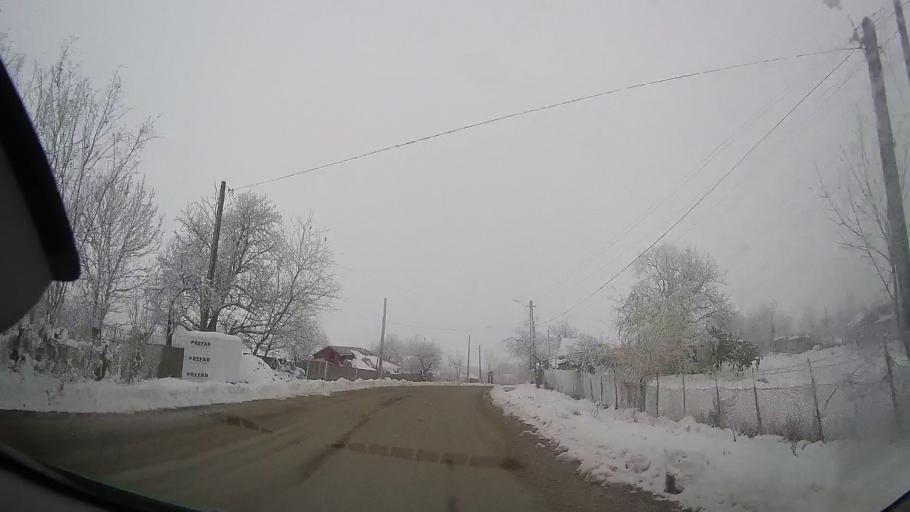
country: RO
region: Iasi
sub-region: Comuna Tansa
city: Tansa
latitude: 46.9128
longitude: 27.2259
